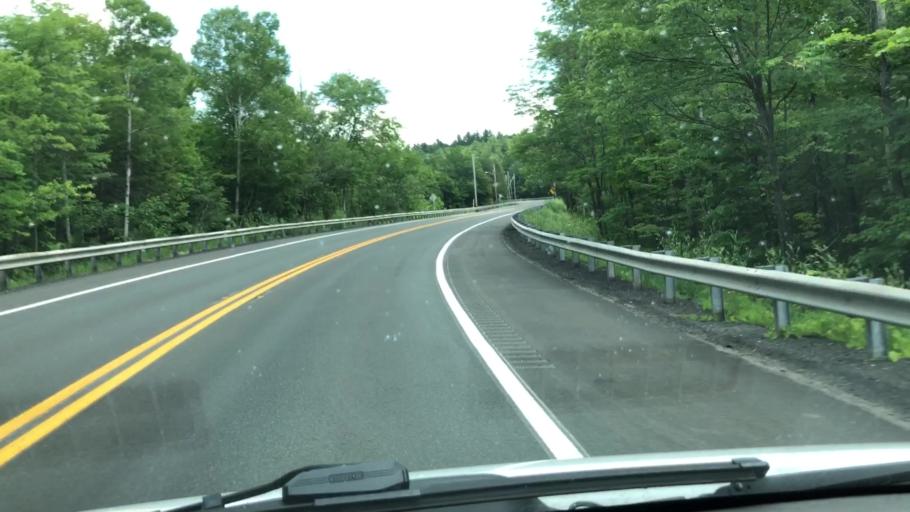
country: US
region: Massachusetts
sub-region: Hampshire County
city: Chesterfield
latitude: 42.4556
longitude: -72.8507
